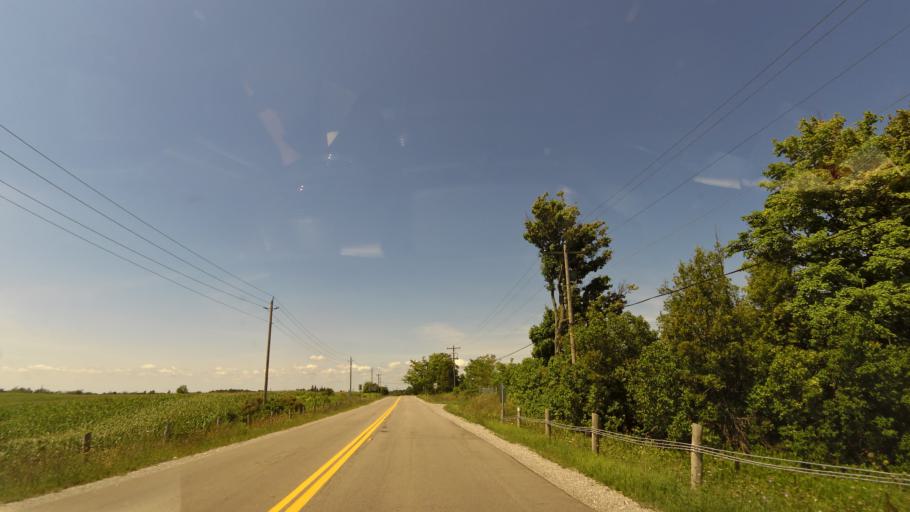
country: CA
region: Ontario
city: Ancaster
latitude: 43.1614
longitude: -79.9366
